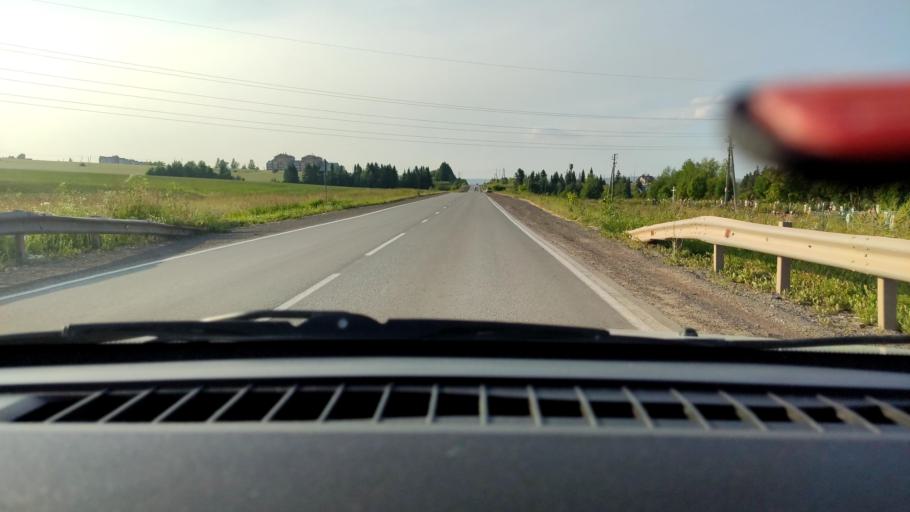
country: RU
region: Perm
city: Lobanovo
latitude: 57.8532
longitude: 56.2962
